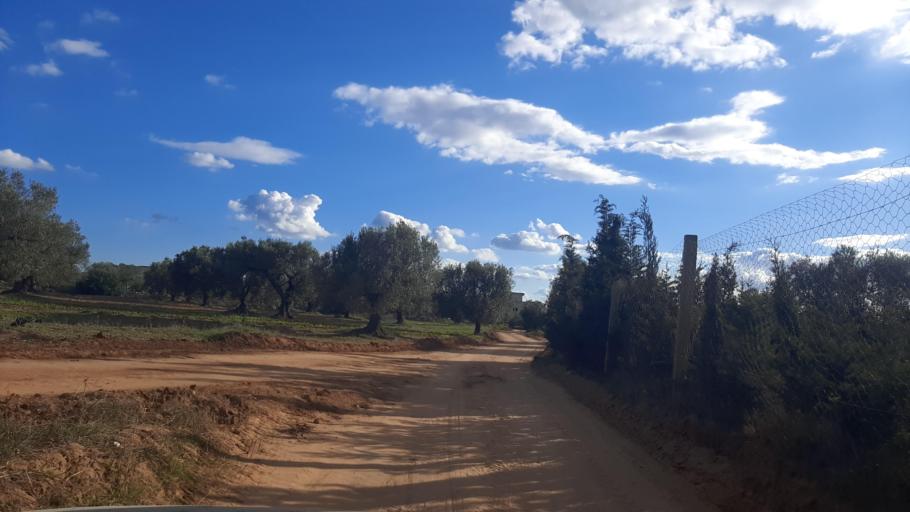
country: TN
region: Nabul
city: Al Hammamat
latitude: 36.4293
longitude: 10.5063
